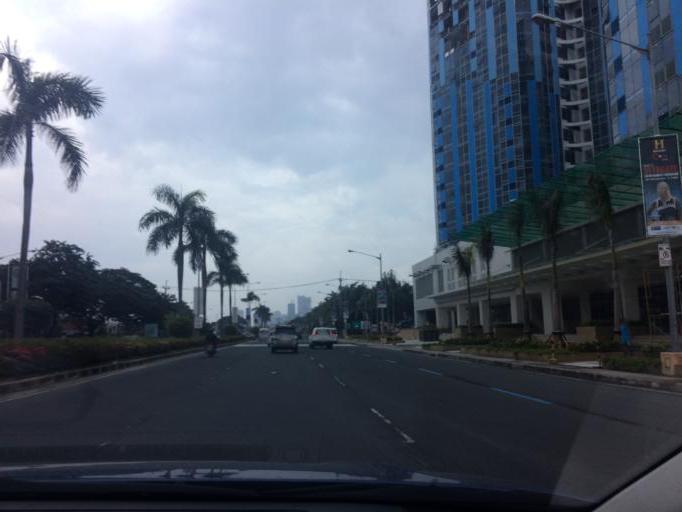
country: PH
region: Metro Manila
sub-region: Makati City
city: Makati City
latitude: 14.5395
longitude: 120.9886
